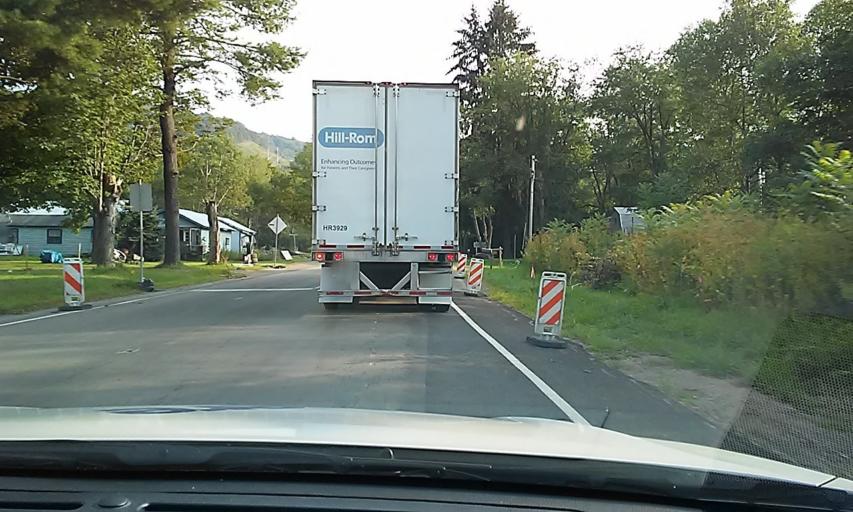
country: US
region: Pennsylvania
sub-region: McKean County
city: Smethport
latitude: 41.7494
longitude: -78.5267
